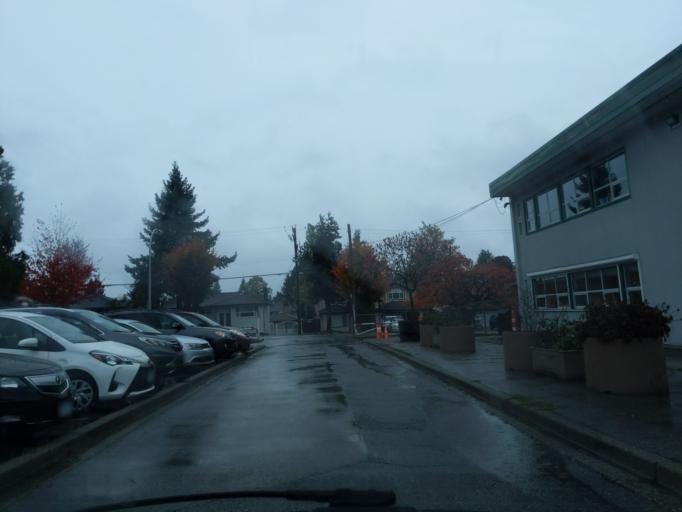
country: CA
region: British Columbia
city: New Westminster
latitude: 49.1949
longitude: -122.8593
